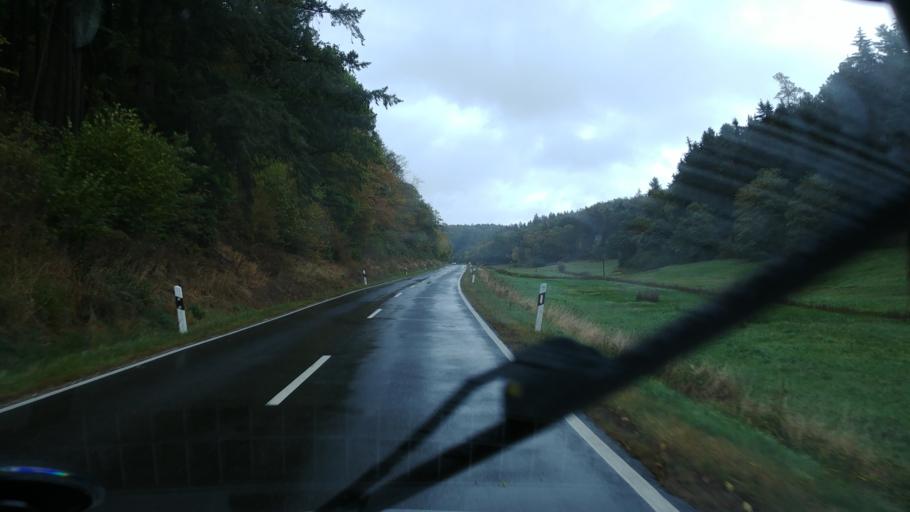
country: DE
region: Hesse
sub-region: Regierungsbezirk Darmstadt
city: Bad Schwalbach
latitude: 50.1459
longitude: 8.0953
